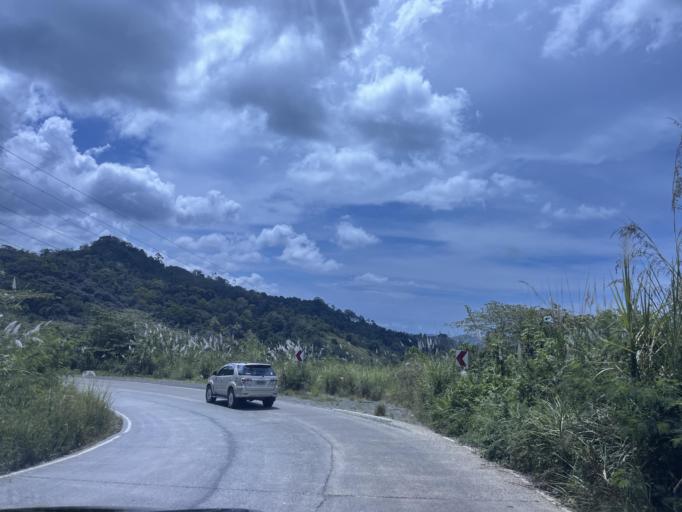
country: PH
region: Northern Mindanao
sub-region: Province of Bukidnon
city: Dalirig
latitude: 8.3590
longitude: 124.9115
